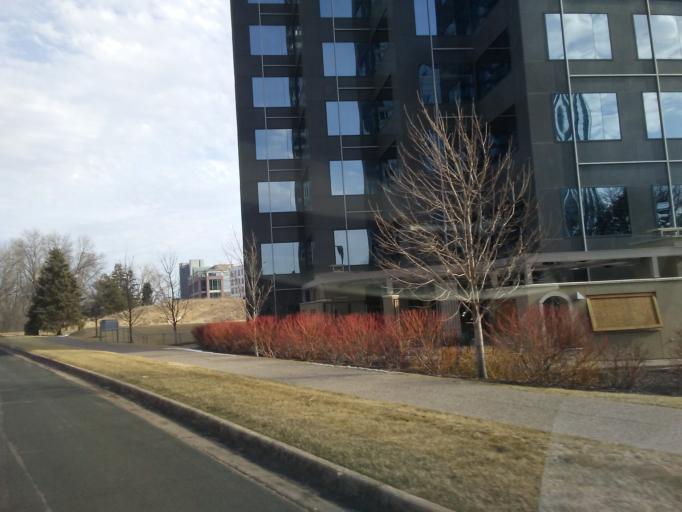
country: US
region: Minnesota
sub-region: Hennepin County
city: Edina
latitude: 44.8543
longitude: -93.3560
